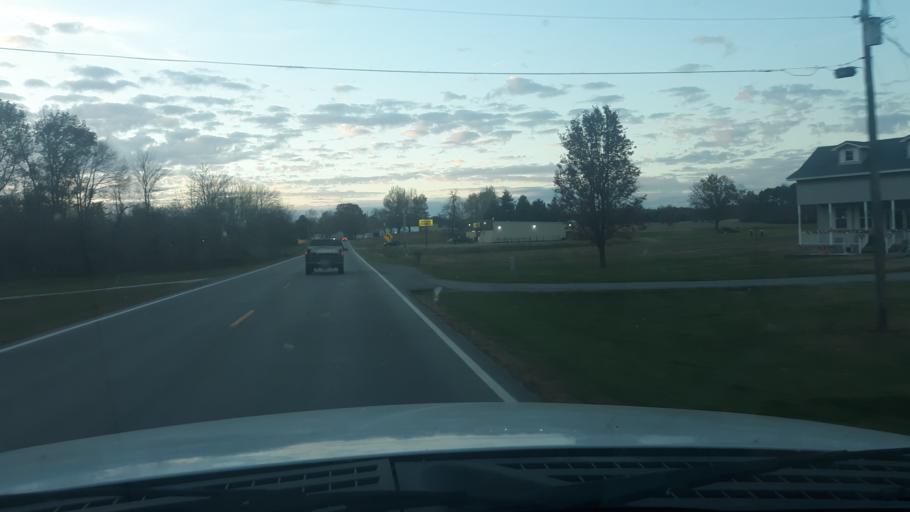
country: US
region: Illinois
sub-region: Saline County
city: Harrisburg
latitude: 37.8388
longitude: -88.5986
